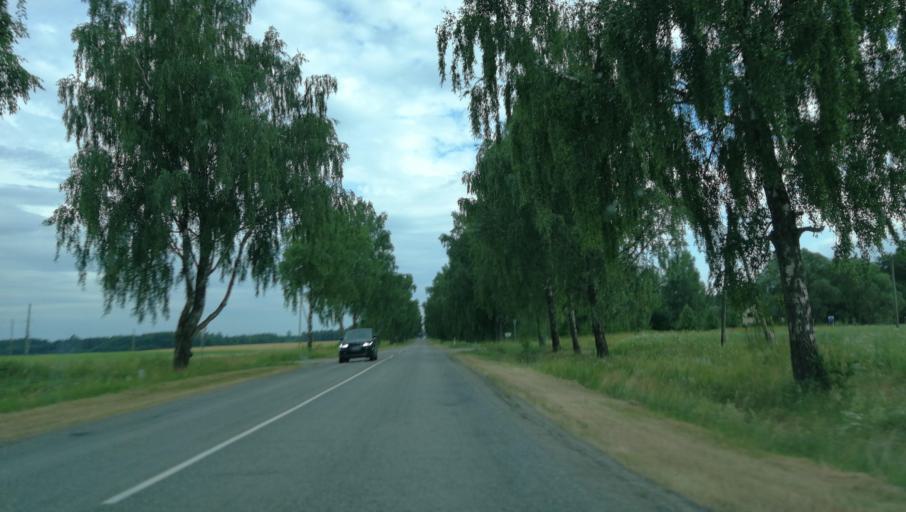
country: LV
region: Valmieras Rajons
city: Valmiera
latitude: 57.6336
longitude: 25.4468
